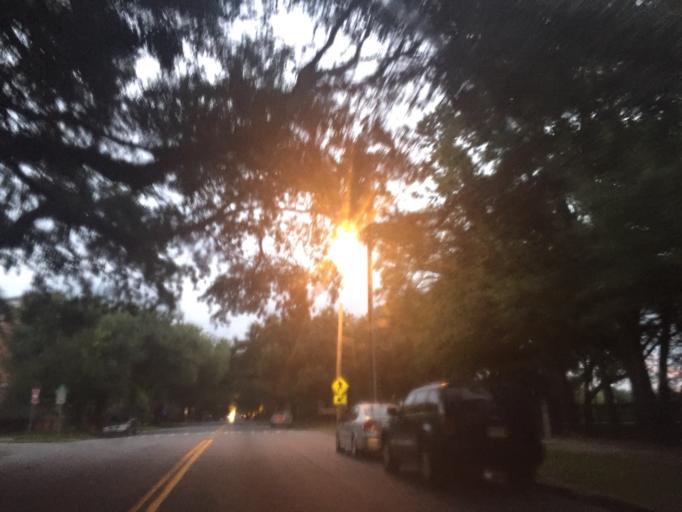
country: US
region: Georgia
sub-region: Chatham County
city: Savannah
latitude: 32.0676
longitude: -81.0883
